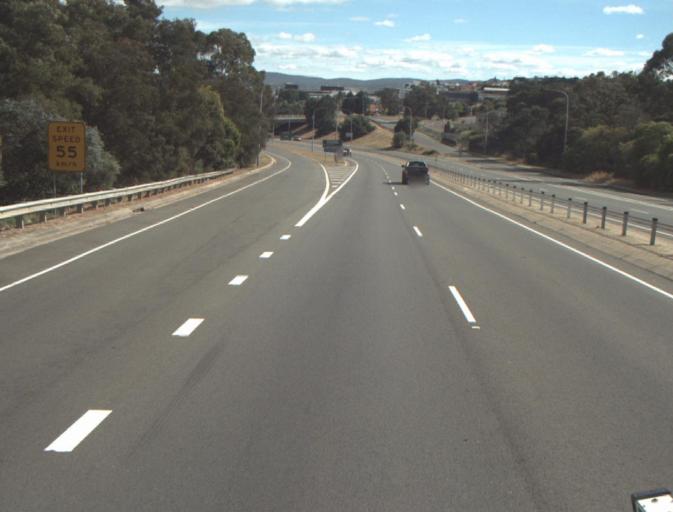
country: AU
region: Tasmania
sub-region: Launceston
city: West Launceston
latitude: -41.4577
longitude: 147.1427
